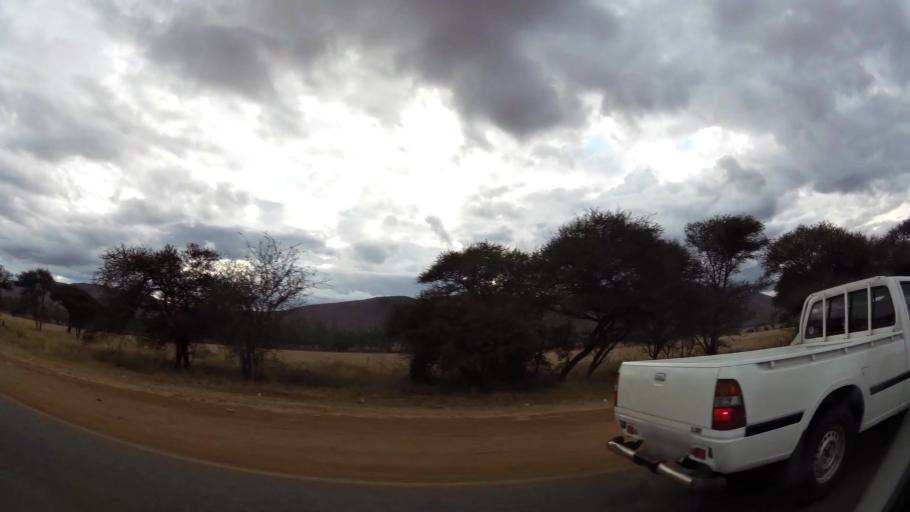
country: ZA
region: Limpopo
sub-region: Waterberg District Municipality
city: Mokopane
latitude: -24.2675
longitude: 28.9827
